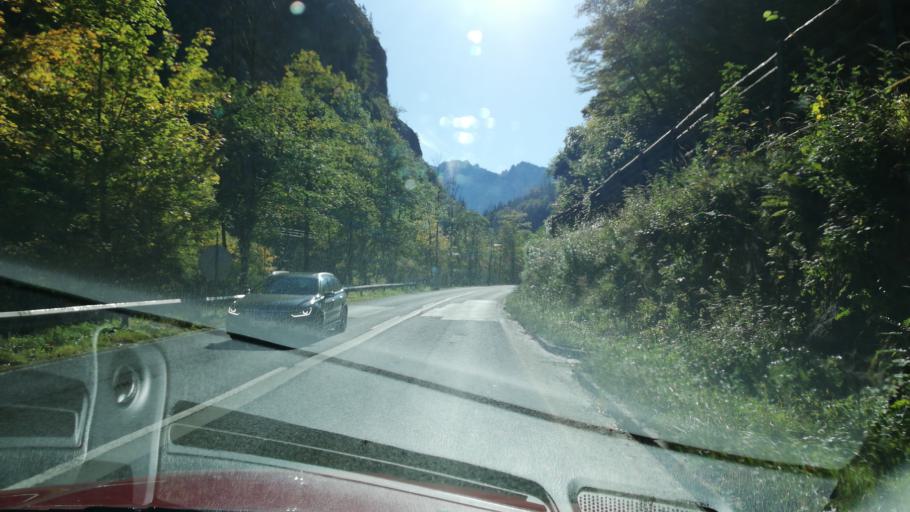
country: AT
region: Styria
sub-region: Politischer Bezirk Leoben
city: Hieflau
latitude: 47.5927
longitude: 14.7518
